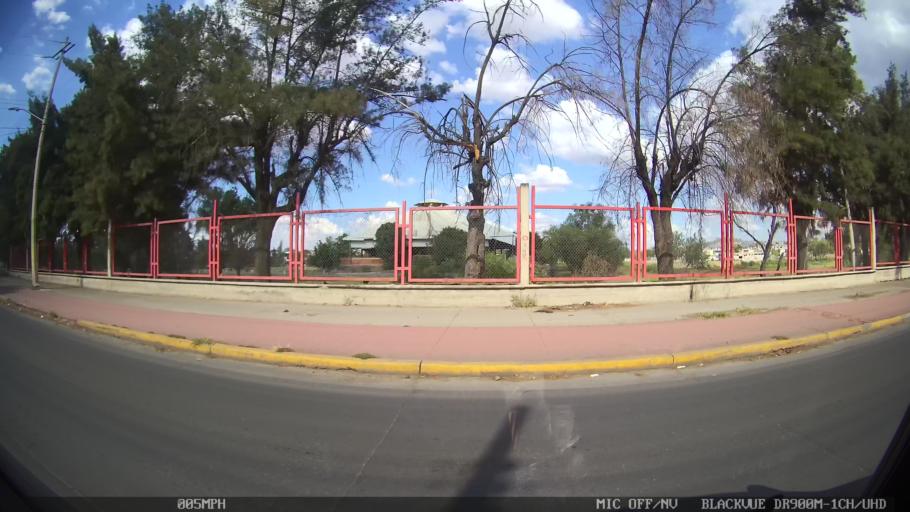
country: MX
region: Jalisco
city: Tlaquepaque
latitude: 20.6546
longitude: -103.2712
